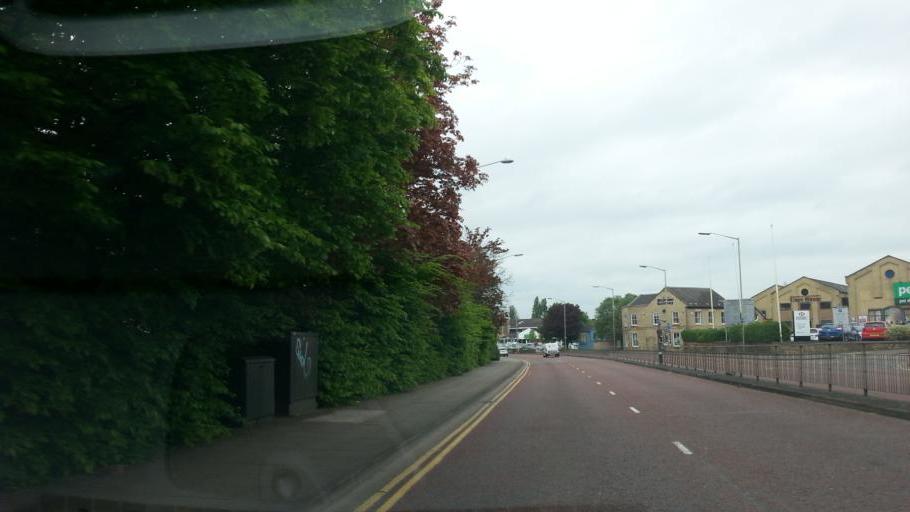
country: GB
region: England
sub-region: Peterborough
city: Peterborough
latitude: 52.5715
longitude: -0.2466
